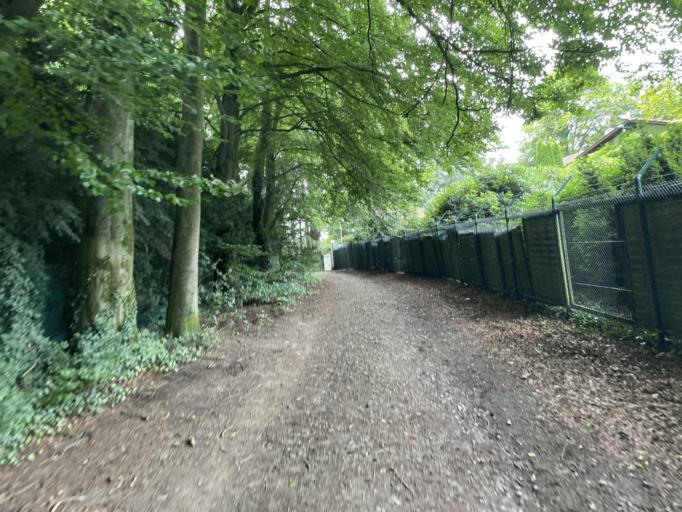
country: DE
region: North Rhine-Westphalia
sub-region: Regierungsbezirk Dusseldorf
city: Heiligenhaus
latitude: 51.3759
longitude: 6.9528
